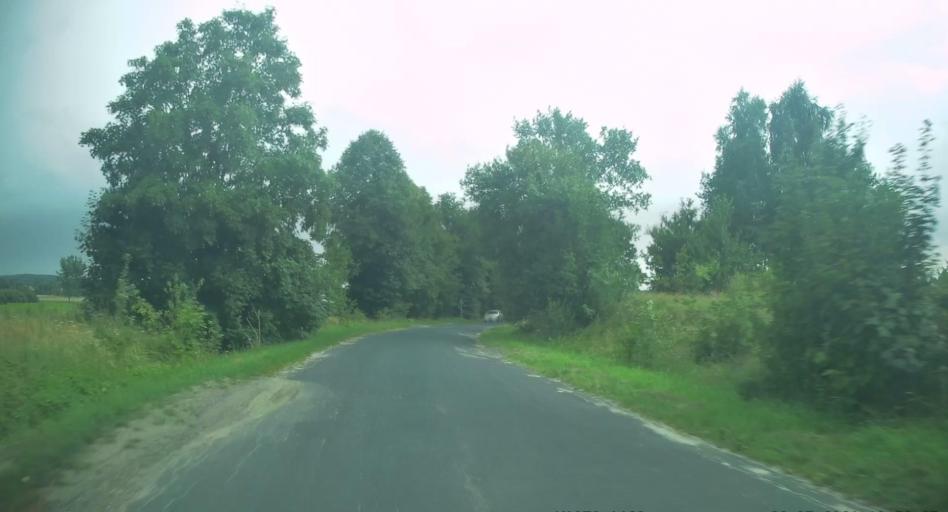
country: PL
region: Lodz Voivodeship
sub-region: Powiat rawski
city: Rawa Mazowiecka
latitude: 51.7556
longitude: 20.1880
